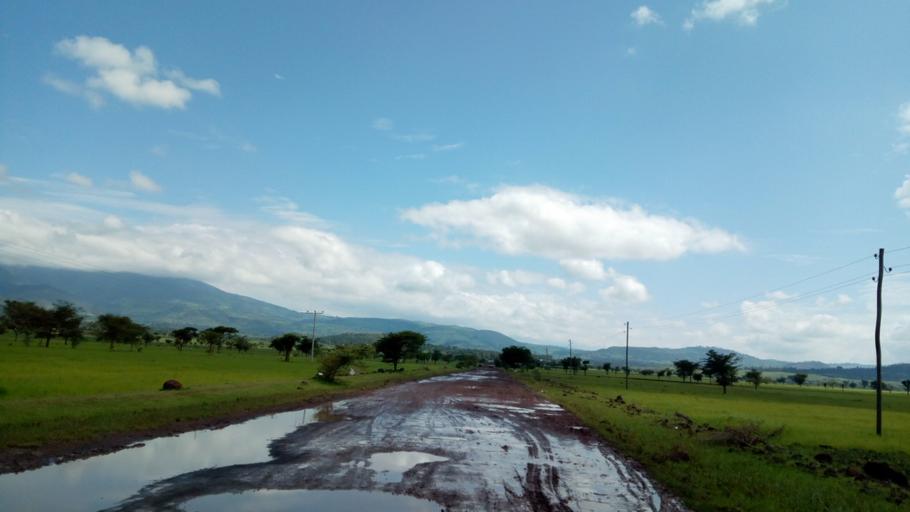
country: ET
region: Oromiya
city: Bishoftu
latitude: 8.8077
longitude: 39.0039
